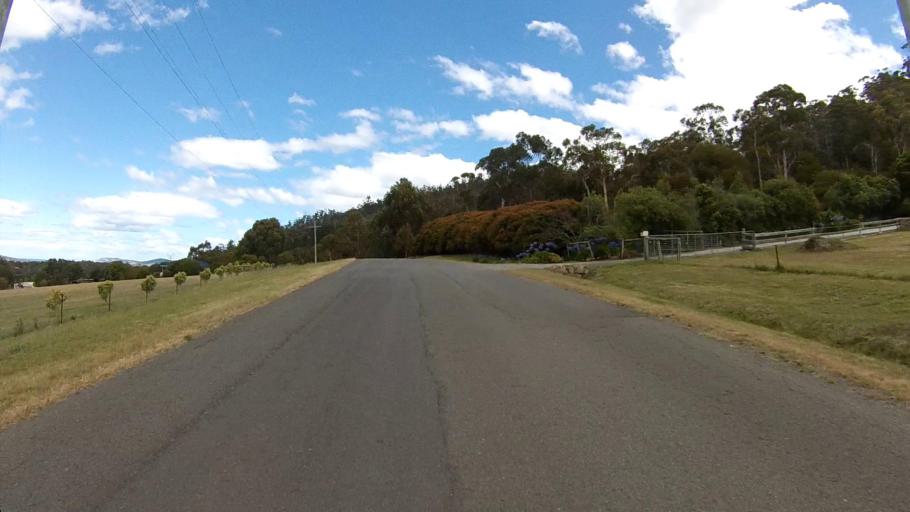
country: AU
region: Tasmania
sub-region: Clarence
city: Acton Park
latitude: -42.8631
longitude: 147.4699
